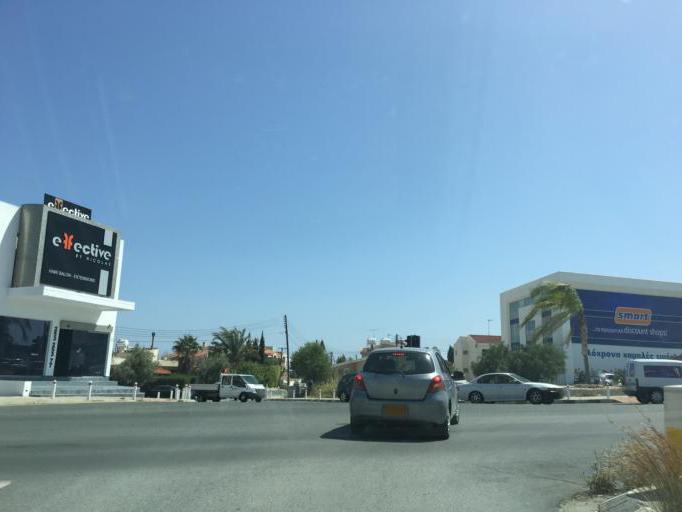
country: CY
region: Limassol
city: Mouttagiaka
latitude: 34.7038
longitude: 33.0816
